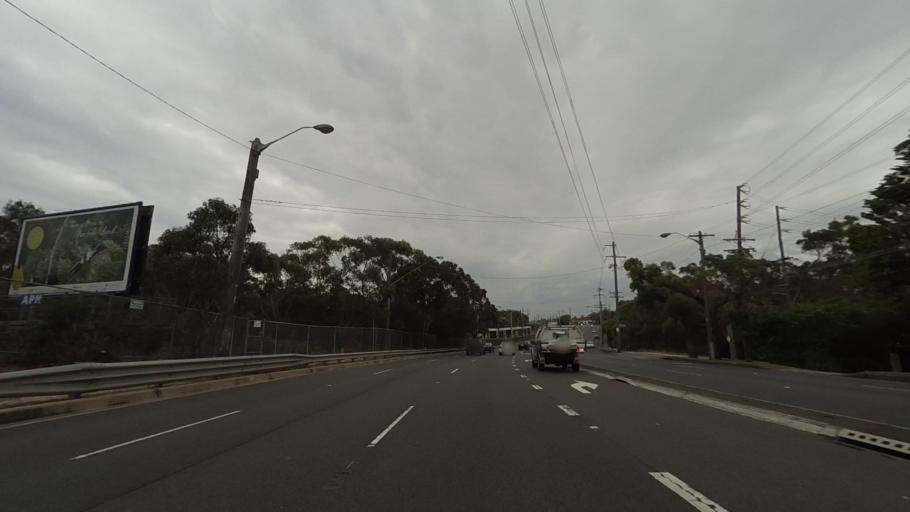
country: AU
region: New South Wales
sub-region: Sutherland Shire
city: Engadine
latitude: -34.0625
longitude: 151.0222
